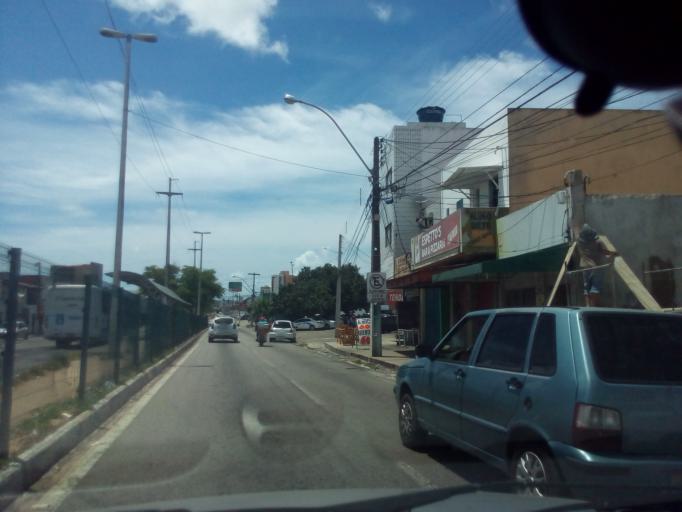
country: BR
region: Rio Grande do Norte
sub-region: Natal
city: Natal
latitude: -5.8061
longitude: -35.2236
